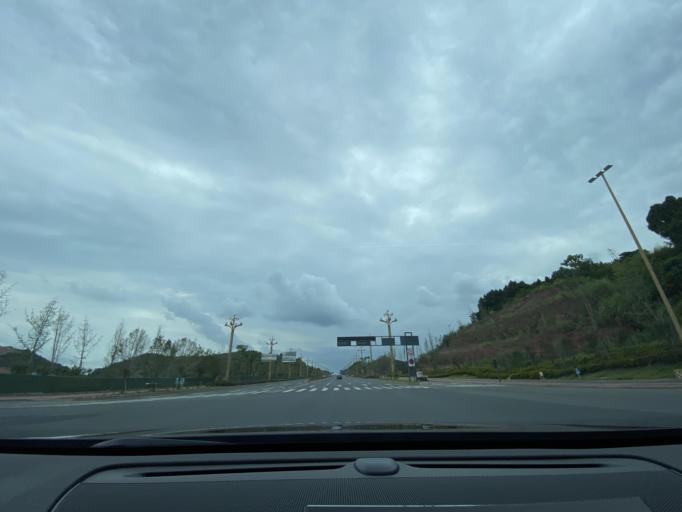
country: CN
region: Sichuan
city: Jiancheng
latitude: 30.4558
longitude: 104.4958
